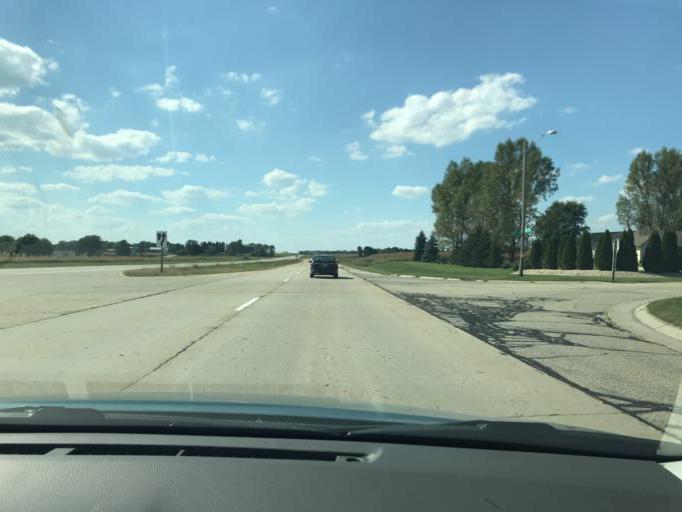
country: US
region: Wisconsin
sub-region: Kenosha County
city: Powers Lake
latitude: 42.5827
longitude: -88.2721
